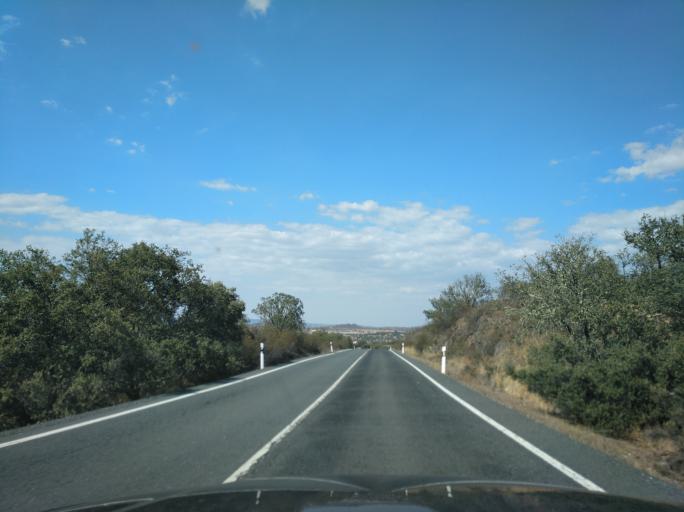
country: ES
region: Andalusia
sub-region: Provincia de Huelva
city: Cabezas Rubias
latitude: 37.6800
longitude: -7.1076
